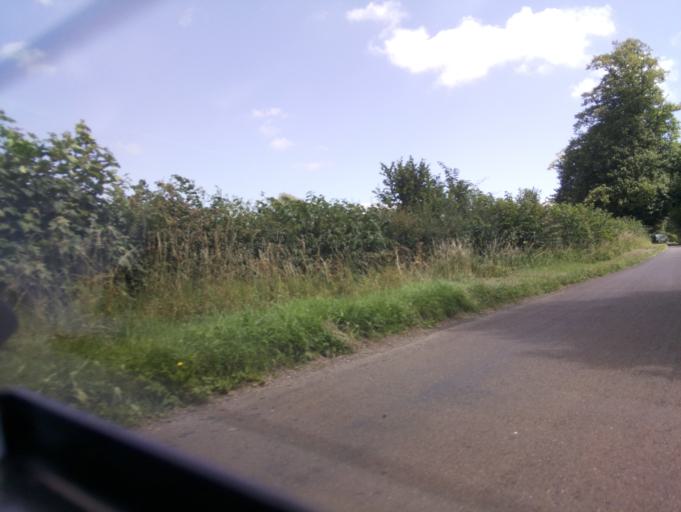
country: GB
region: England
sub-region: Wiltshire
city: Luckington
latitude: 51.5381
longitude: -2.2088
